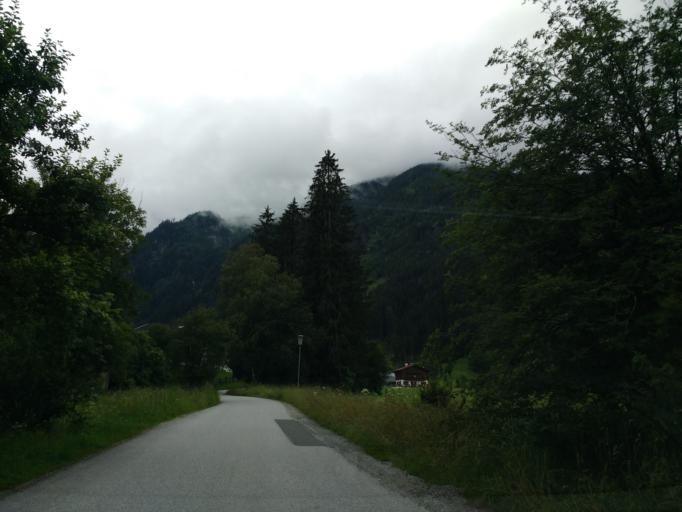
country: AT
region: Salzburg
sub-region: Politischer Bezirk Zell am See
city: Wald im Pinzgau
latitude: 47.2339
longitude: 12.2508
